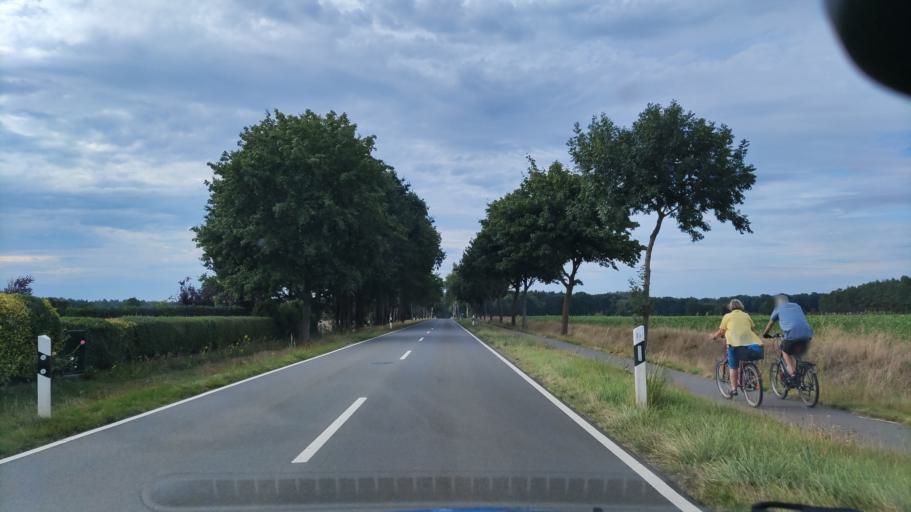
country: DE
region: Lower Saxony
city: Walsrode
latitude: 52.8347
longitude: 9.6296
